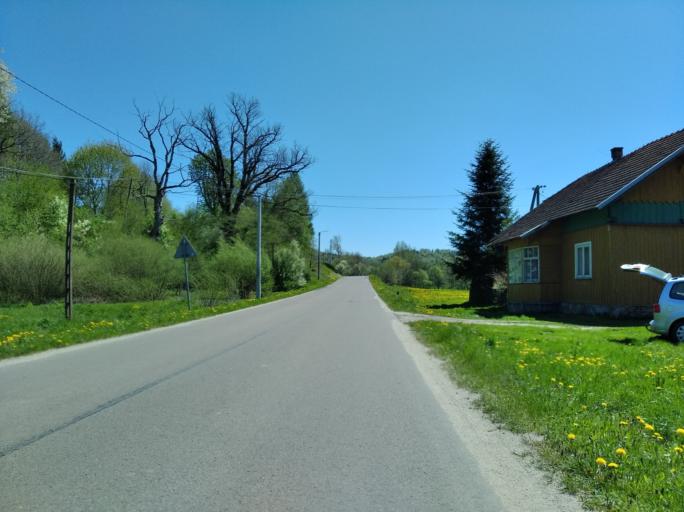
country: PL
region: Subcarpathian Voivodeship
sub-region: Powiat debicki
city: Brzostek
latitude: 49.9185
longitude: 21.4035
